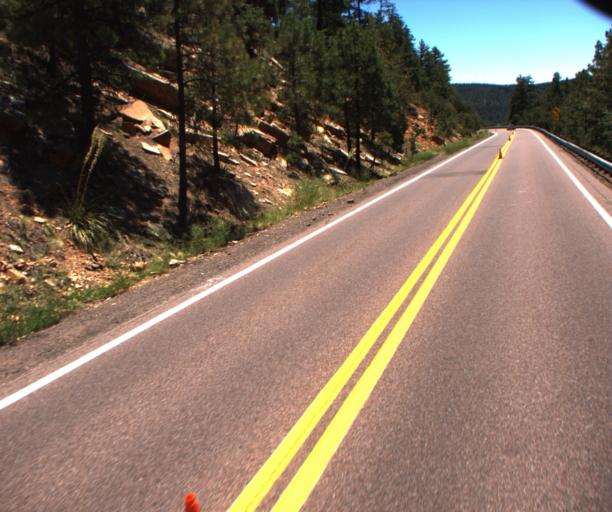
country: US
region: Arizona
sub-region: Gila County
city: Pine
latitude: 34.4205
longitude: -111.5009
